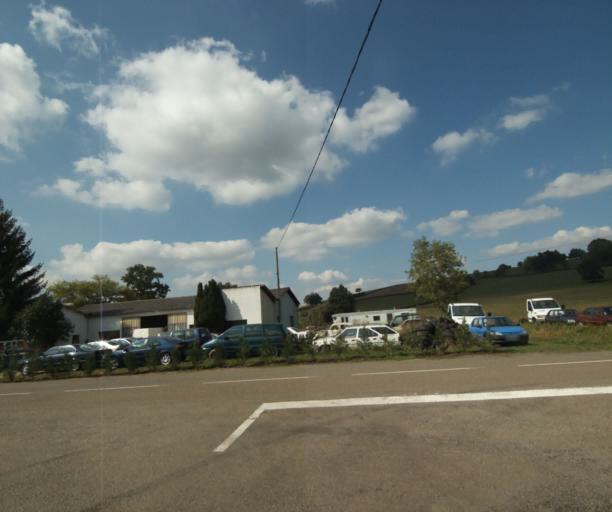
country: FR
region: Bourgogne
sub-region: Departement de Saone-et-Loire
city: Charolles
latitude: 46.3671
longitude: 4.2379
